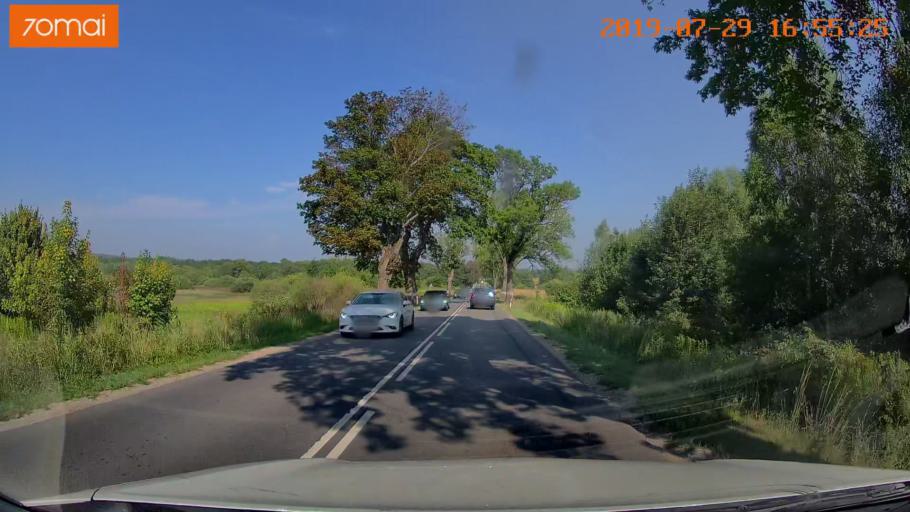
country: RU
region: Kaliningrad
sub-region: Gorod Svetlogorsk
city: Svetlogorsk
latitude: 54.8135
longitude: 20.1512
